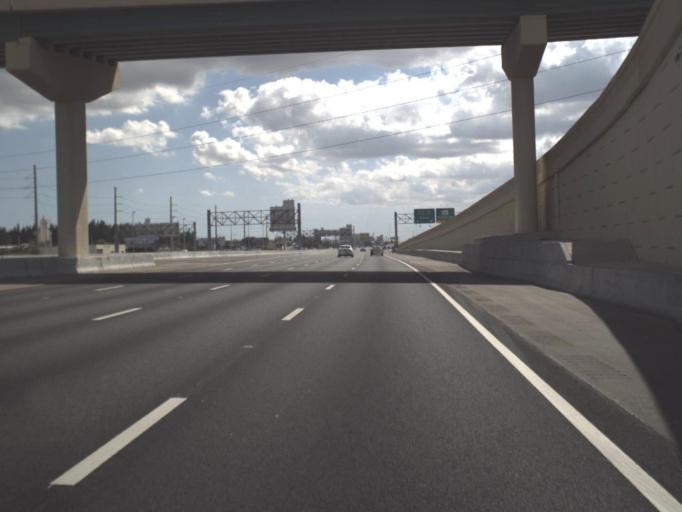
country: US
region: Florida
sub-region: Broward County
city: Broadview Park
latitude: 26.0835
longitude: -80.2165
